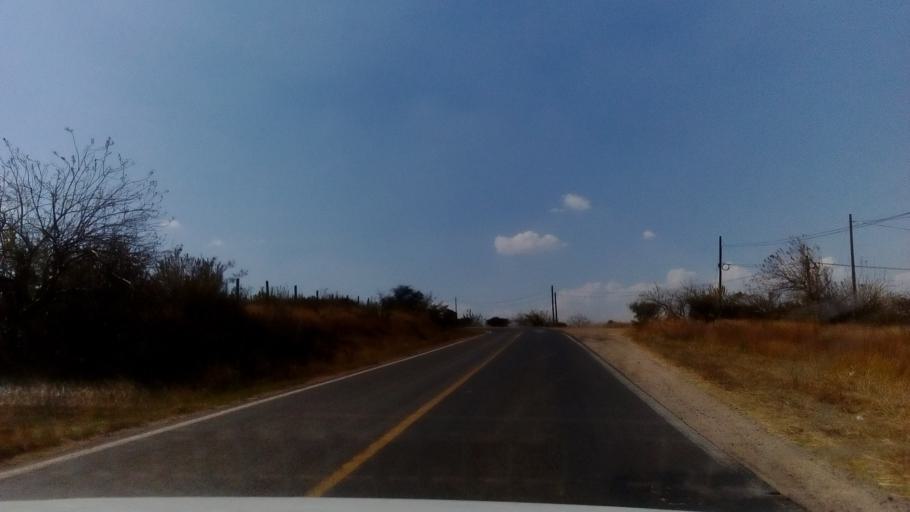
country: MX
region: Guanajuato
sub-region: Silao de la Victoria
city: San Francisco (Banos de Agua Caliente)
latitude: 21.0743
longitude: -101.4885
